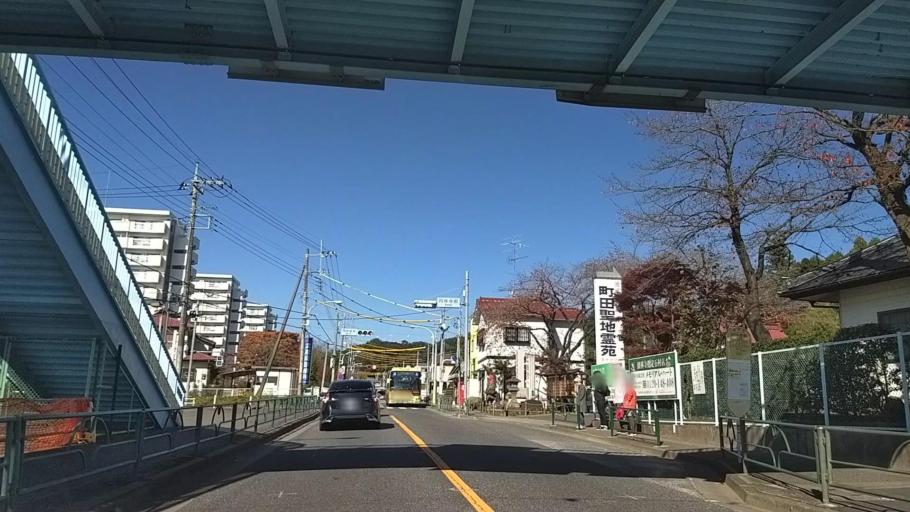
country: JP
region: Tokyo
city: Hachioji
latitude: 35.6075
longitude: 139.3015
